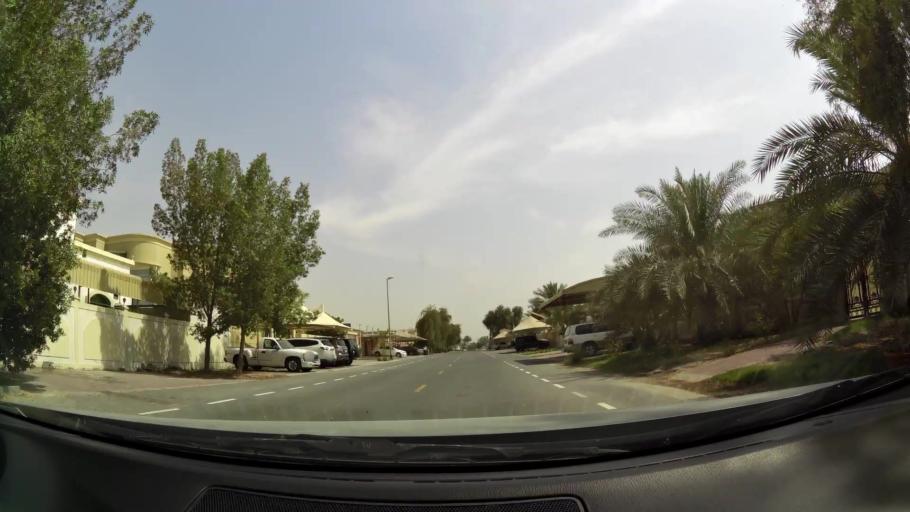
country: AE
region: Ash Shariqah
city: Sharjah
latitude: 25.2418
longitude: 55.4468
